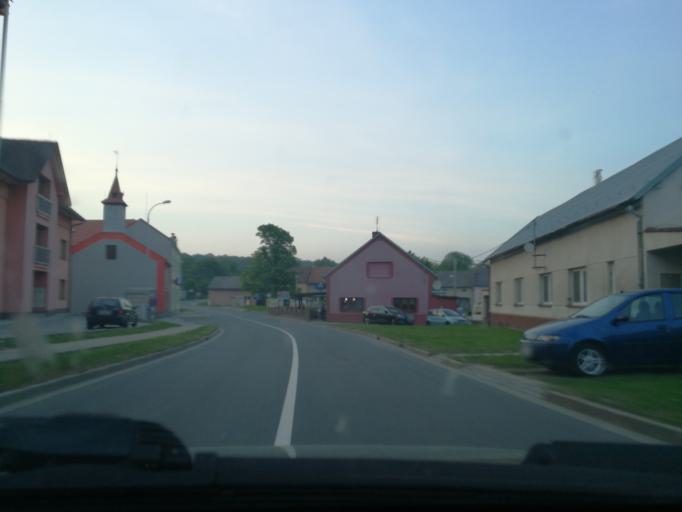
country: CZ
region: Zlin
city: Tlumacov
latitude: 49.2760
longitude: 17.5487
